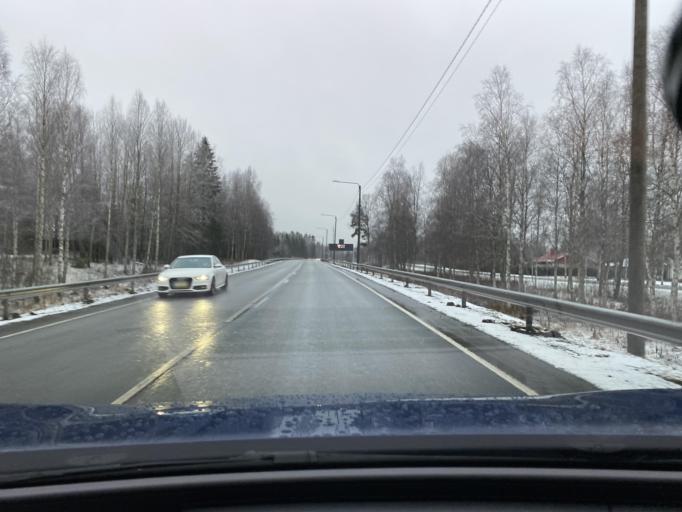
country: FI
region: Northern Ostrobothnia
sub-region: Oulu
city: Kiiminki
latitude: 65.1310
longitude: 25.7954
